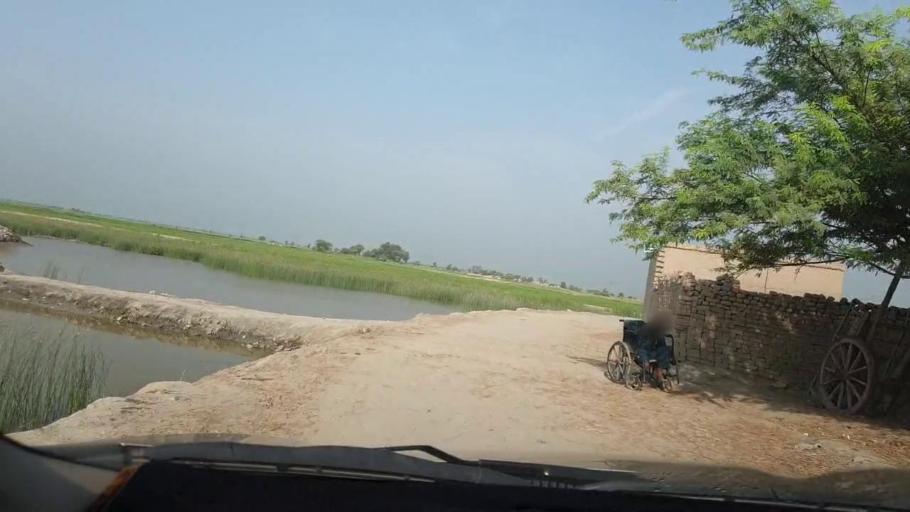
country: PK
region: Sindh
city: Goth Garelo
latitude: 27.4662
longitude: 68.0821
